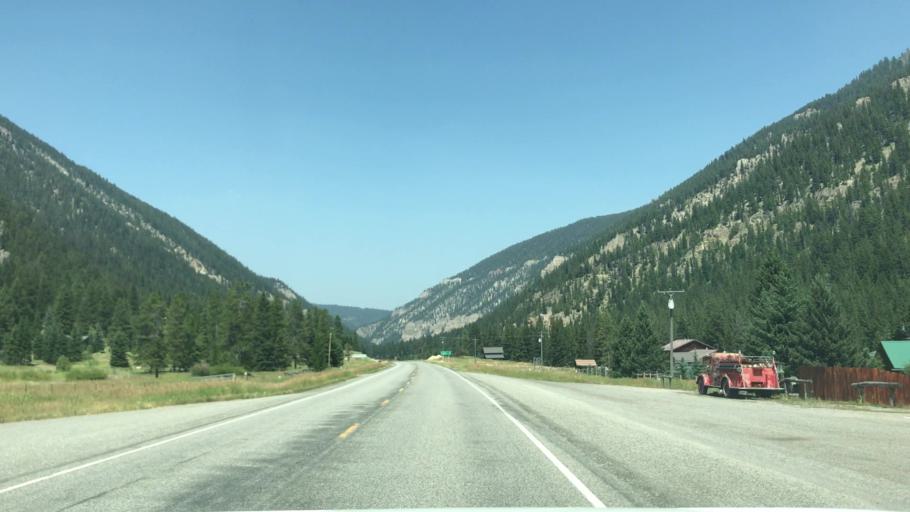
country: US
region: Montana
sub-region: Gallatin County
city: Big Sky
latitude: 45.1162
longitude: -111.2256
